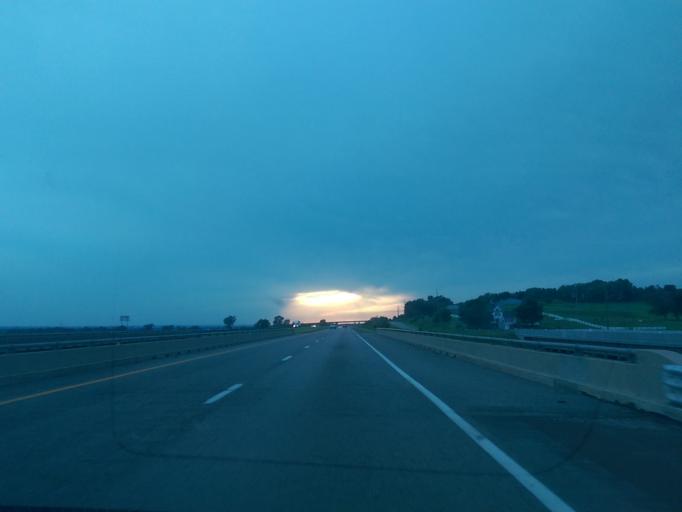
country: US
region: Missouri
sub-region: Holt County
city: Mound City
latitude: 40.1556
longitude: -95.2642
